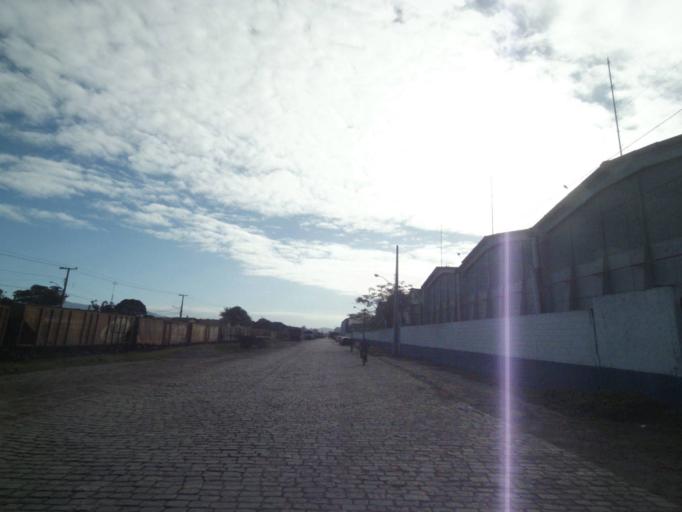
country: BR
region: Parana
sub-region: Paranagua
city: Paranagua
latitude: -25.5232
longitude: -48.5281
